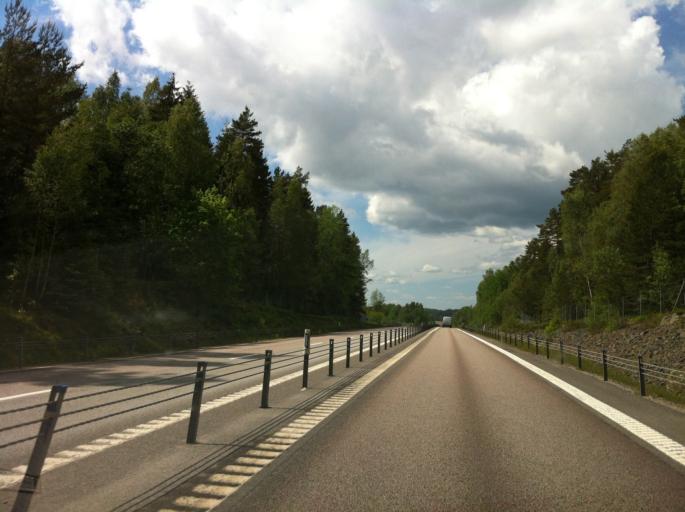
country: SE
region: Vaermland
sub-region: Saffle Kommun
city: Saeffle
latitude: 59.1249
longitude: 12.8660
